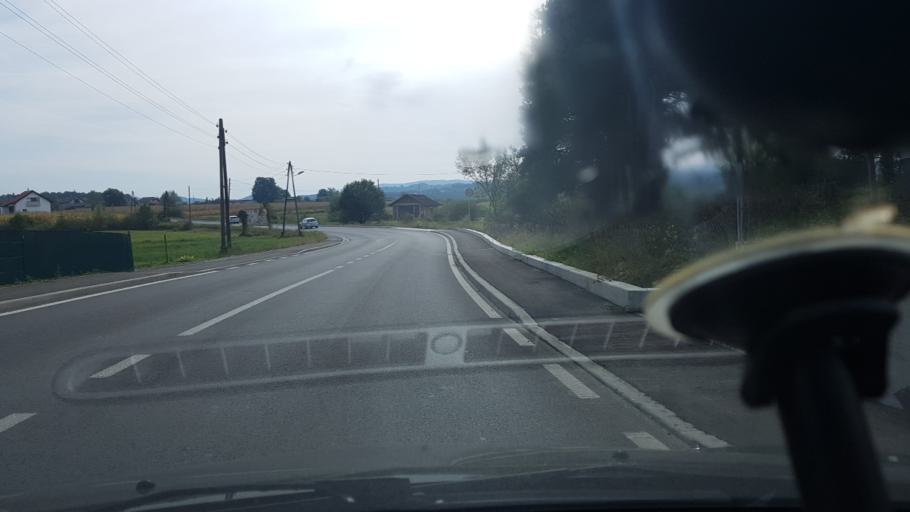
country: HR
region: Krapinsko-Zagorska
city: Marija Bistrica
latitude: 46.0502
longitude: 16.1109
